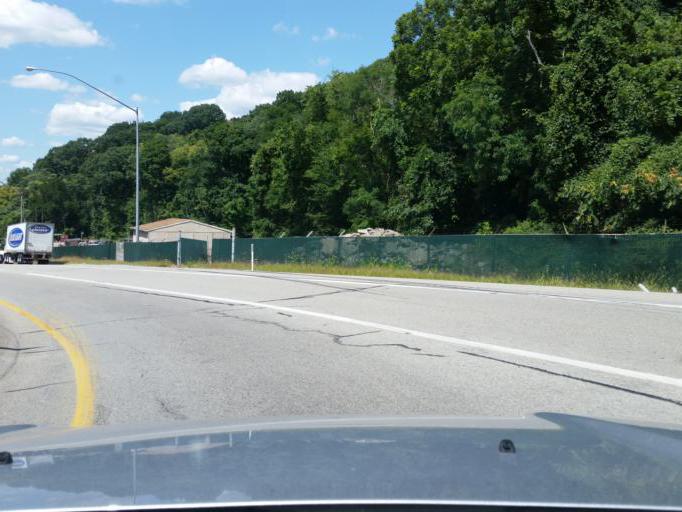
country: US
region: Pennsylvania
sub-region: Allegheny County
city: Homestead
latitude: 40.4293
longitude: -79.9321
